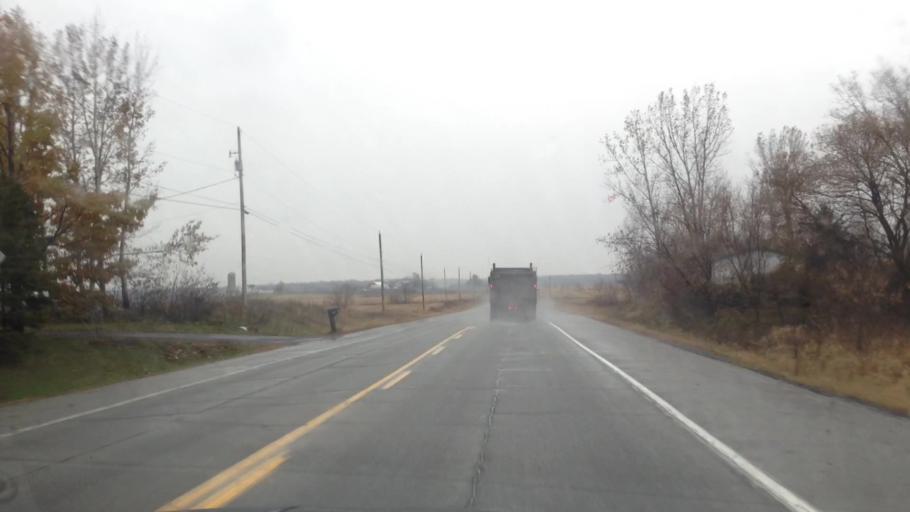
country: CA
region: Ontario
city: Clarence-Rockland
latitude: 45.4131
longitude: -75.4034
